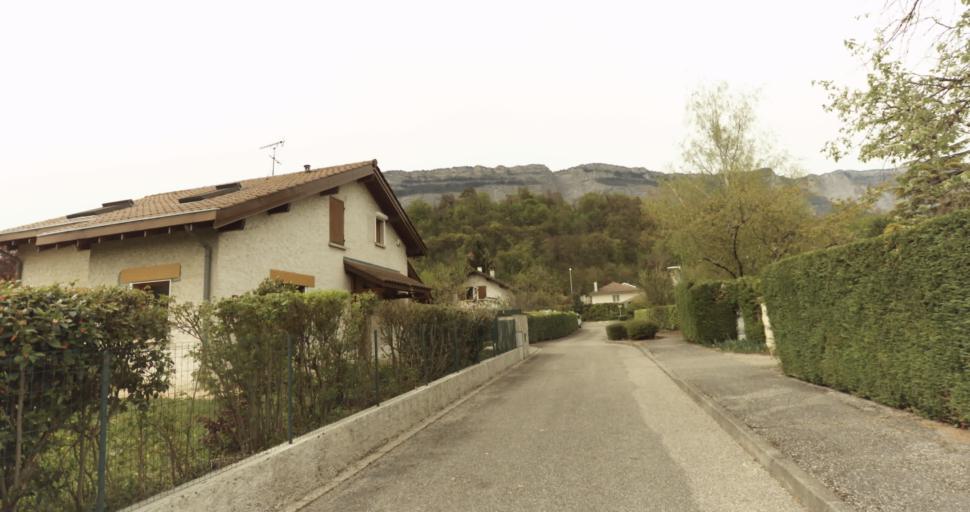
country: FR
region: Rhone-Alpes
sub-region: Departement de l'Isere
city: Montbonnot-Saint-Martin
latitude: 45.2228
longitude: 5.8047
